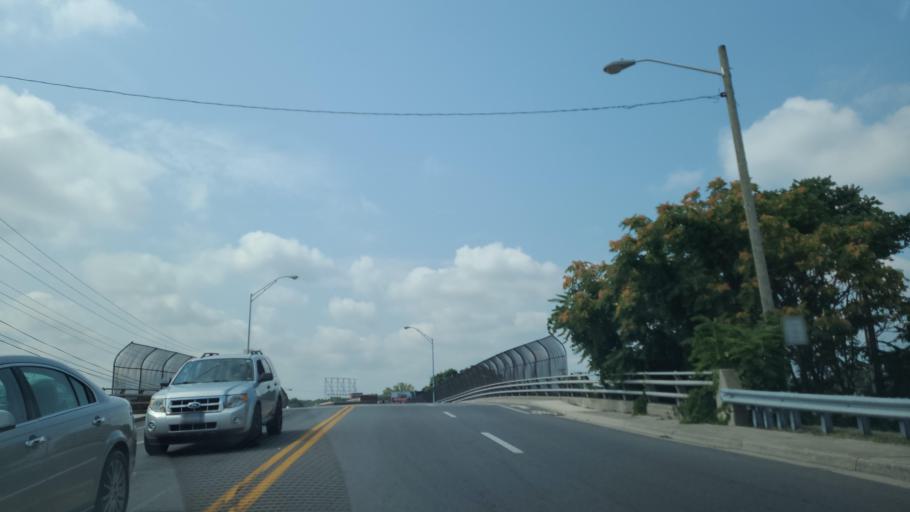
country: US
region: Virginia
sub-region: City of Roanoke
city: Roanoke
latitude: 37.2745
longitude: -79.9493
